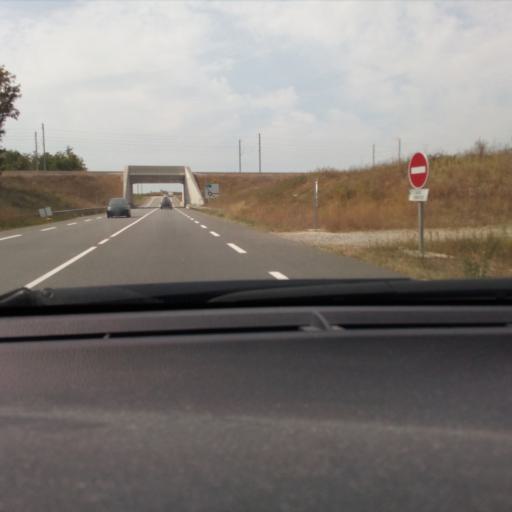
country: FR
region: Poitou-Charentes
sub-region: Departement de la Charente
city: Fleac
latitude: 45.6801
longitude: 0.0761
